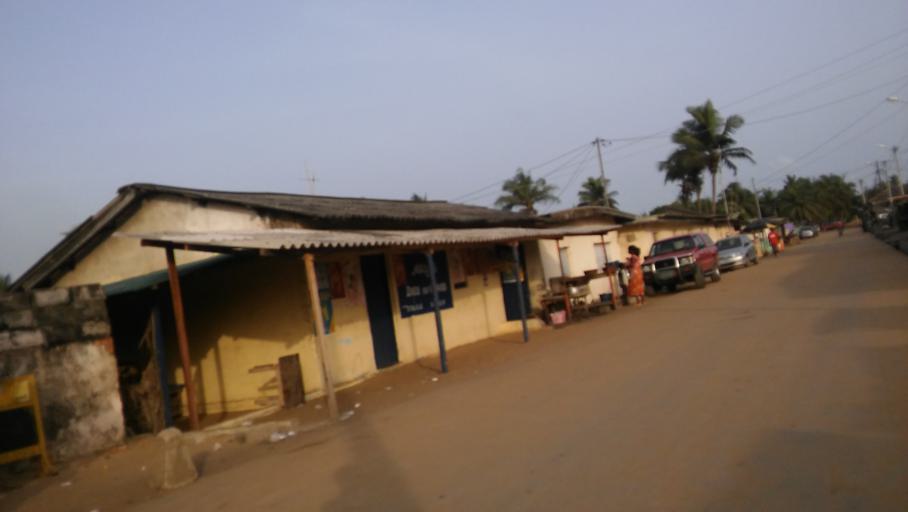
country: CI
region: Sud-Comoe
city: Grand-Bassam
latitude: 5.1945
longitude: -3.7266
